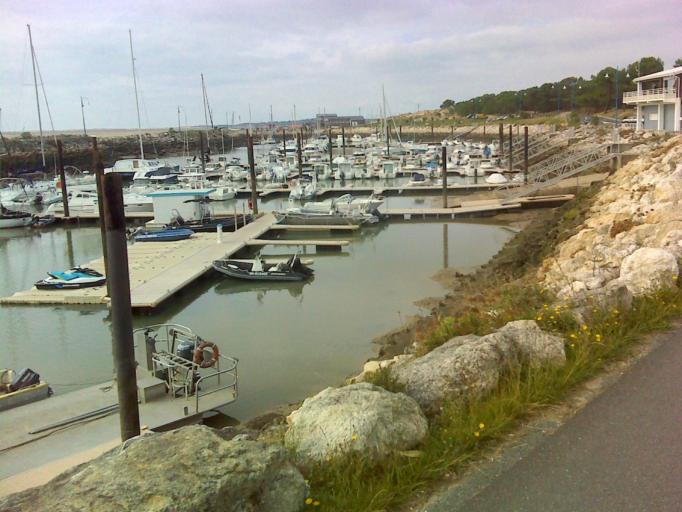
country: FR
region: Poitou-Charentes
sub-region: Departement de la Charente-Maritime
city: Les Mathes
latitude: 45.6839
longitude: -1.1818
